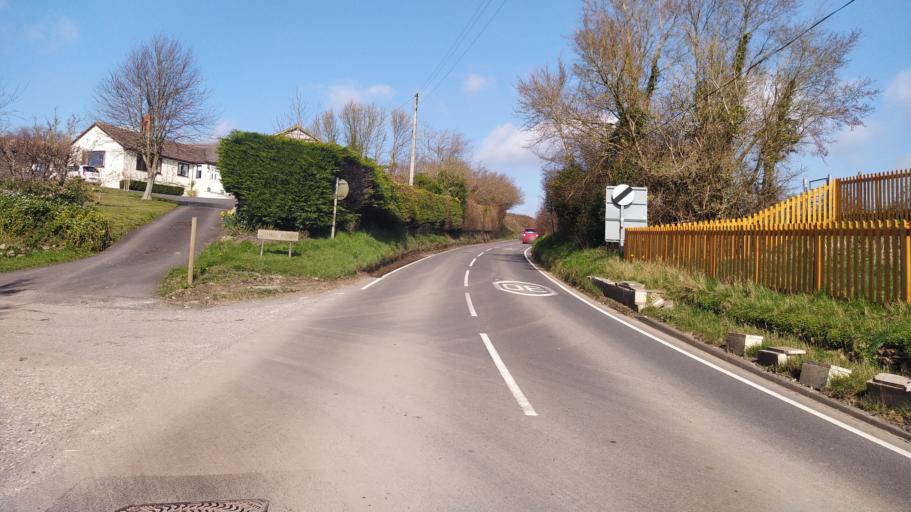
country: GB
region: England
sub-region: Somerset
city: Crewkerne
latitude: 50.8487
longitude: -2.7716
